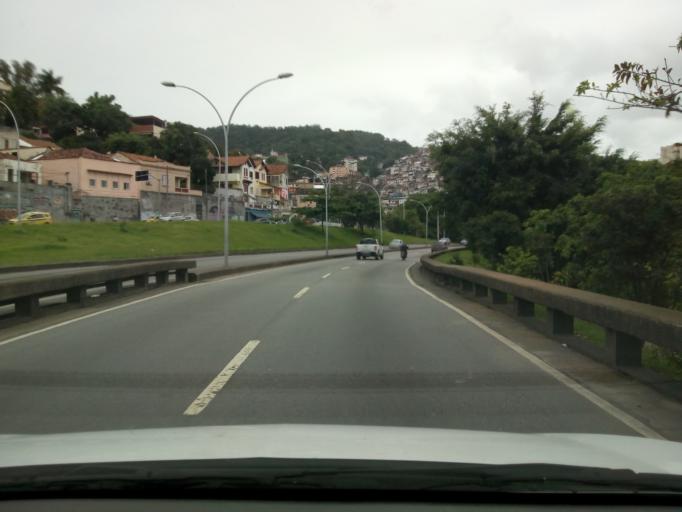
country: BR
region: Rio de Janeiro
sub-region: Rio De Janeiro
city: Rio de Janeiro
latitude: -22.9158
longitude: -43.1944
